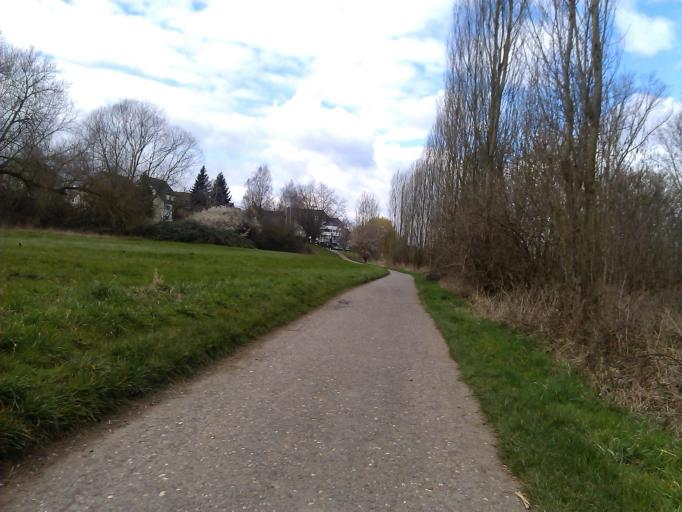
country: DE
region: Rheinland-Pfalz
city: Kaltenengers
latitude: 50.4156
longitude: 7.5528
